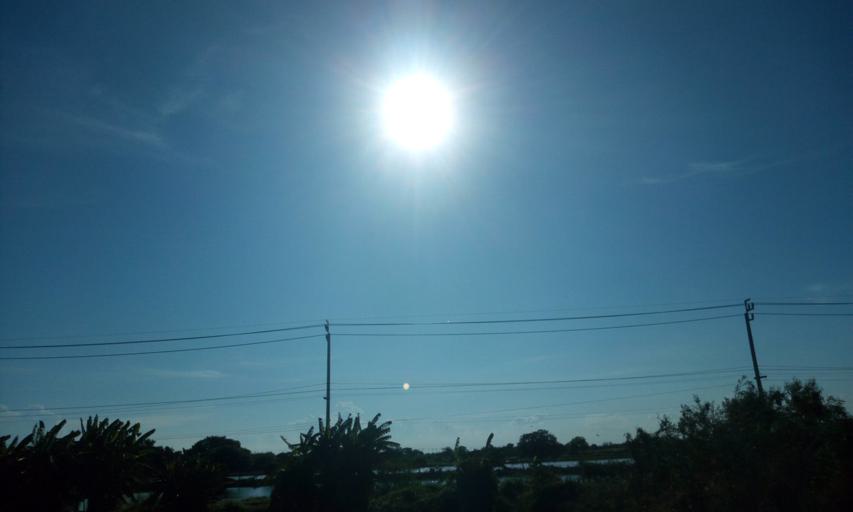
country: TH
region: Samut Prakan
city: Bang Bo District
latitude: 13.5315
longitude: 100.7488
